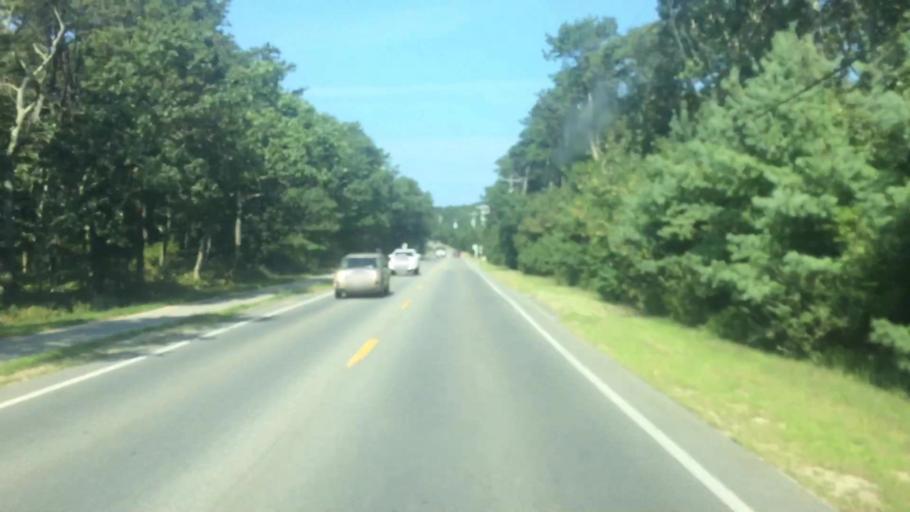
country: US
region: Massachusetts
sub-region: Dukes County
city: Oak Bluffs
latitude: 41.4126
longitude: -70.5762
